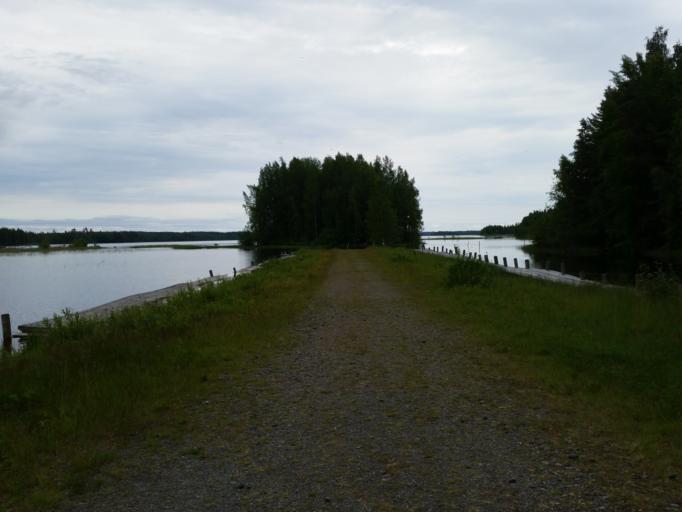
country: FI
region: Northern Savo
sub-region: Sisae-Savo
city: Tervo
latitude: 63.0054
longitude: 26.6899
